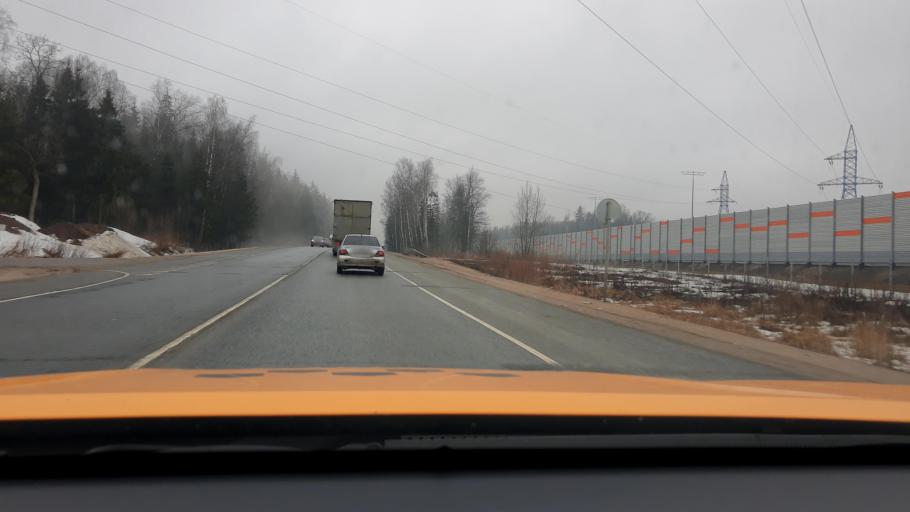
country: RU
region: Moskovskaya
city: Zelenogradskiy
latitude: 56.0885
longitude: 37.9924
